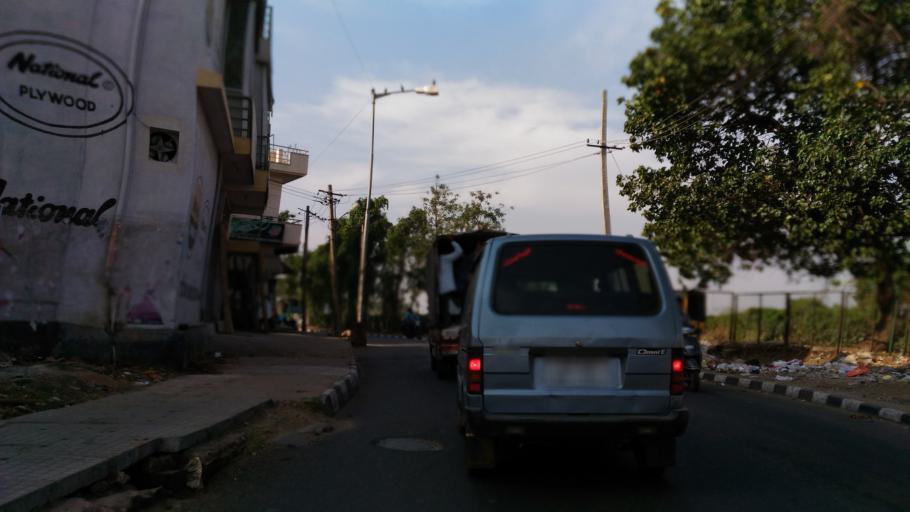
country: IN
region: Karnataka
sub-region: Bangalore Urban
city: Bangalore
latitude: 12.9408
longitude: 77.5342
